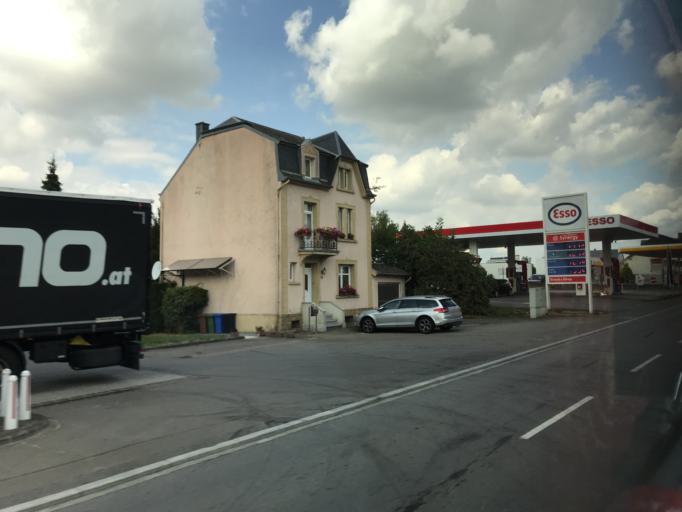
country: LU
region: Luxembourg
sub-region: Canton d'Esch-sur-Alzette
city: Frisange
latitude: 49.5106
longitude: 6.1909
